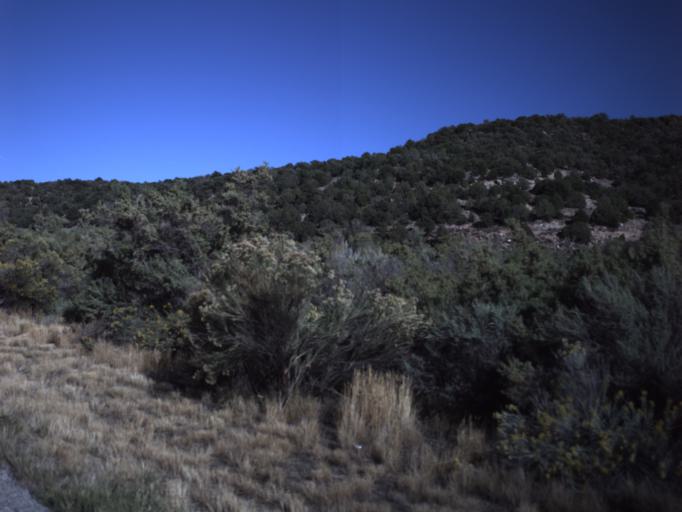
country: US
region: Utah
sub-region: Grand County
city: Moab
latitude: 38.3077
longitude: -109.3597
